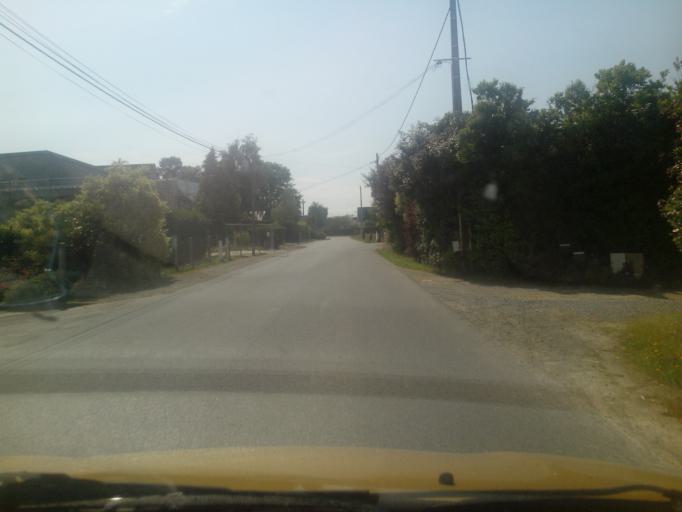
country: FR
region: Brittany
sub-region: Departement d'Ille-et-Vilaine
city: Melesse
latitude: 48.2285
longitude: -1.6971
